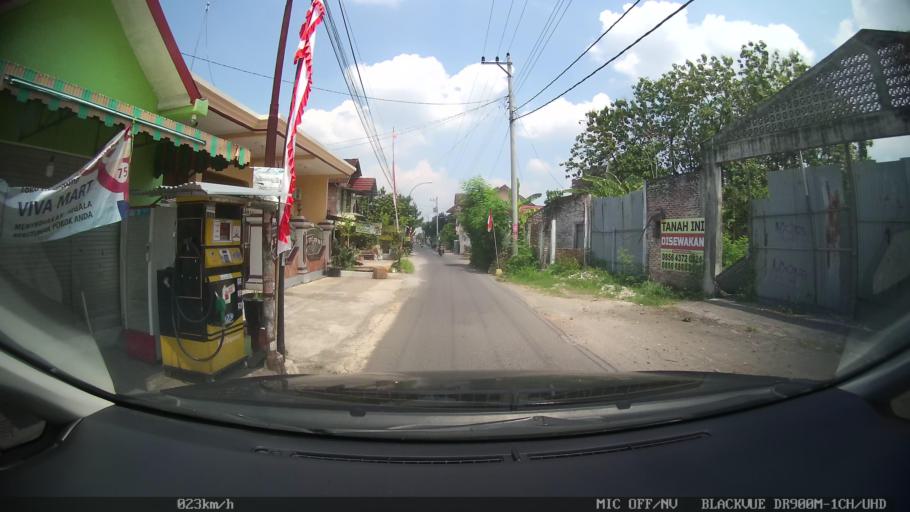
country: ID
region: Daerah Istimewa Yogyakarta
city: Yogyakarta
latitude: -7.8121
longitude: 110.4051
